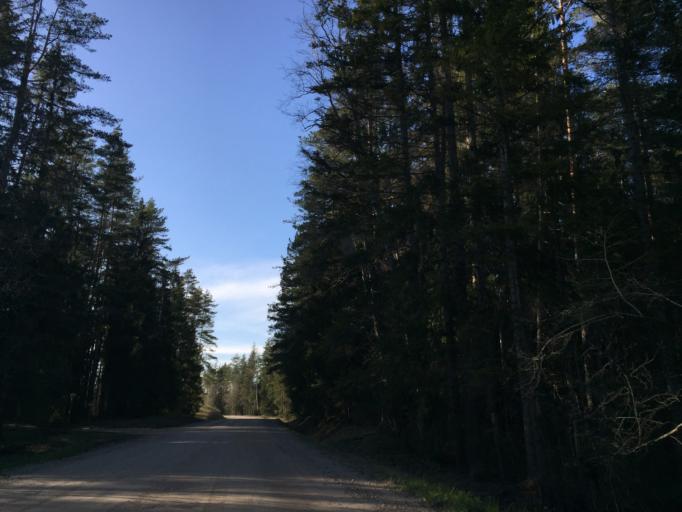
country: LV
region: Valkas Rajons
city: Valka
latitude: 57.7970
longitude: 25.9630
